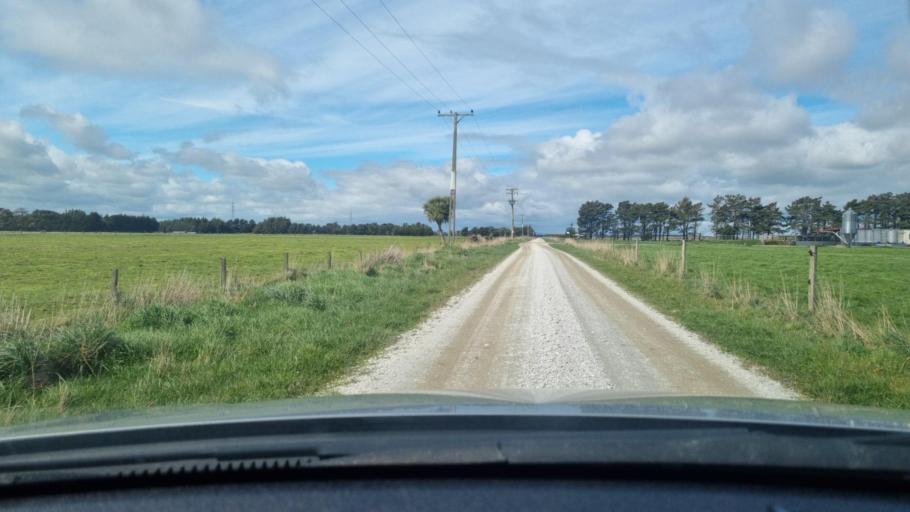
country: NZ
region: Southland
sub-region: Invercargill City
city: Invercargill
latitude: -46.4768
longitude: 168.4232
